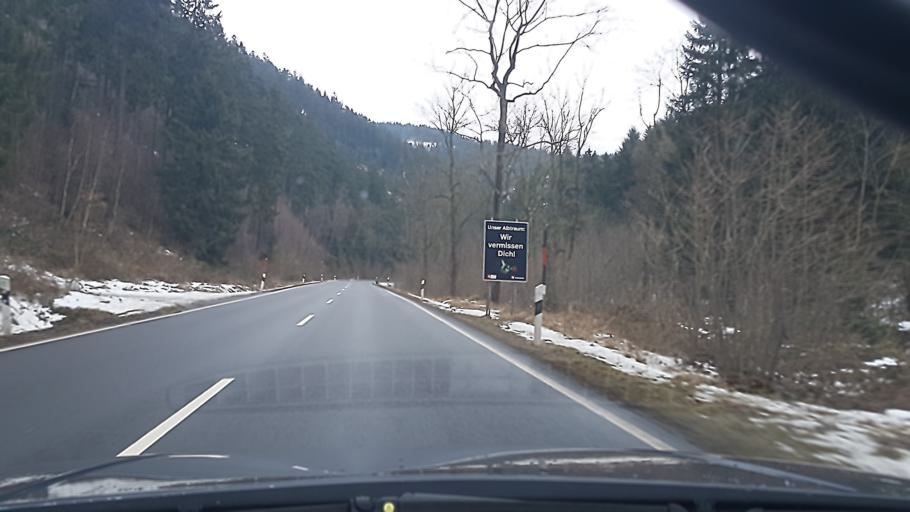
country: DE
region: Lower Saxony
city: Goslar
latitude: 51.8829
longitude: 10.4004
